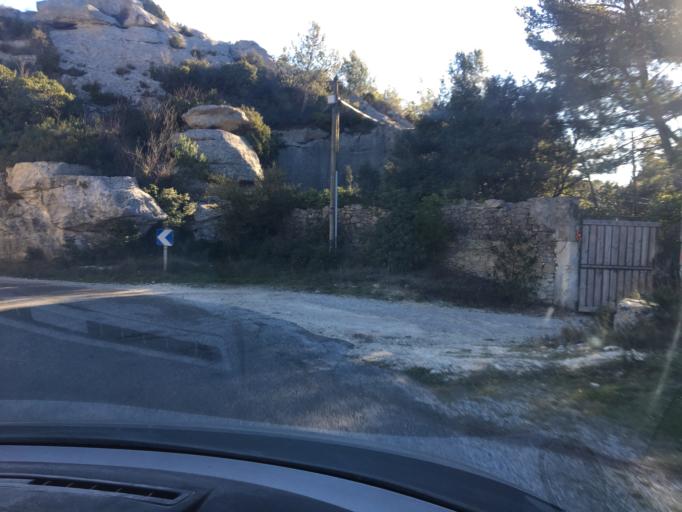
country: FR
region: Provence-Alpes-Cote d'Azur
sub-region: Departement des Bouches-du-Rhone
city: Maussane-les-Alpilles
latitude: 43.7506
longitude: 4.7913
